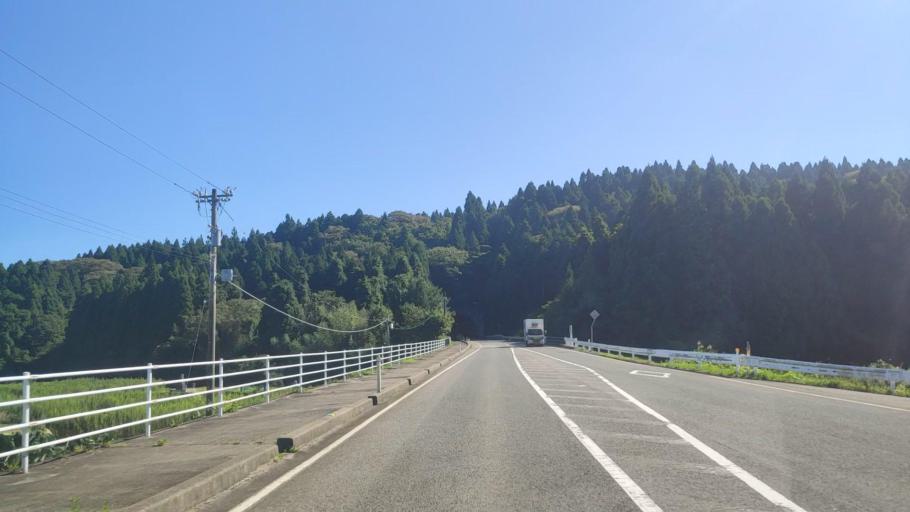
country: JP
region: Ishikawa
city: Nanao
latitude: 37.3863
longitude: 137.2330
